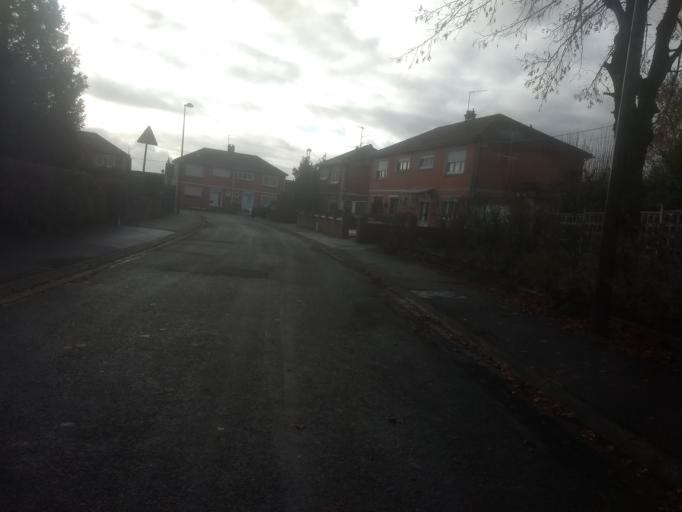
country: FR
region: Nord-Pas-de-Calais
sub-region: Departement du Pas-de-Calais
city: Dainville
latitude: 50.2935
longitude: 2.7307
